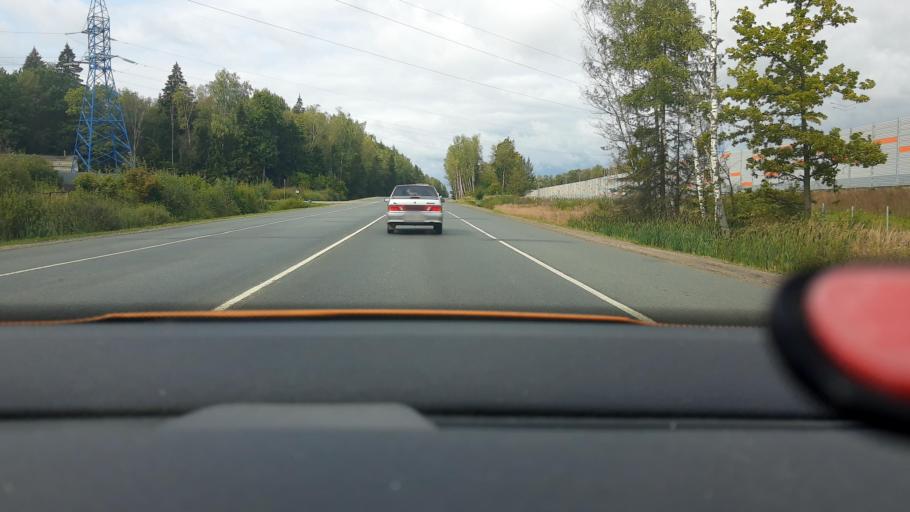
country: RU
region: Moskovskaya
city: Zelenogradskiy
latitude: 56.0882
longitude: 37.9932
